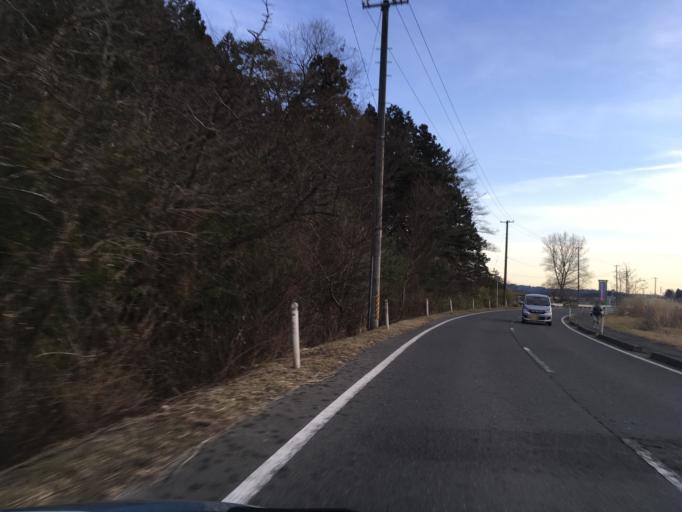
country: JP
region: Miyagi
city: Kogota
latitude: 38.6622
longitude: 141.0734
